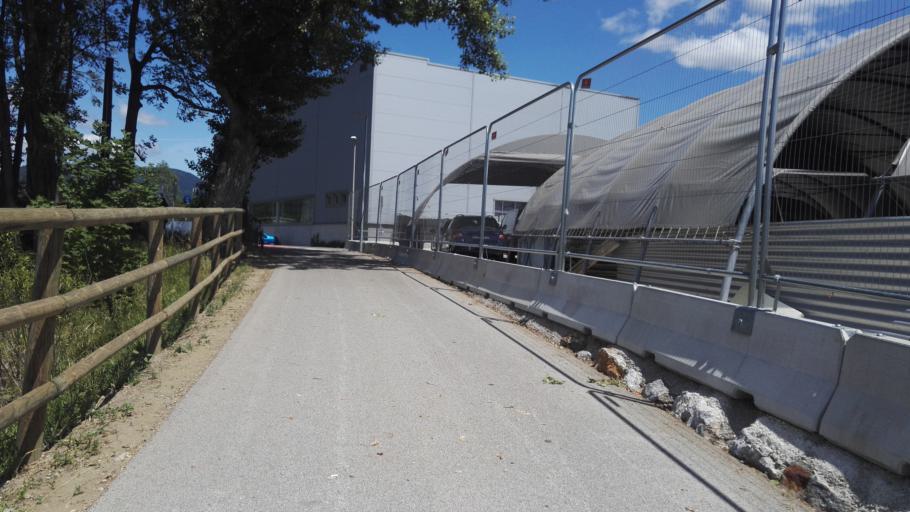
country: AT
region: Styria
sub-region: Graz Stadt
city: Goesting
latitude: 47.1015
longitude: 15.4137
